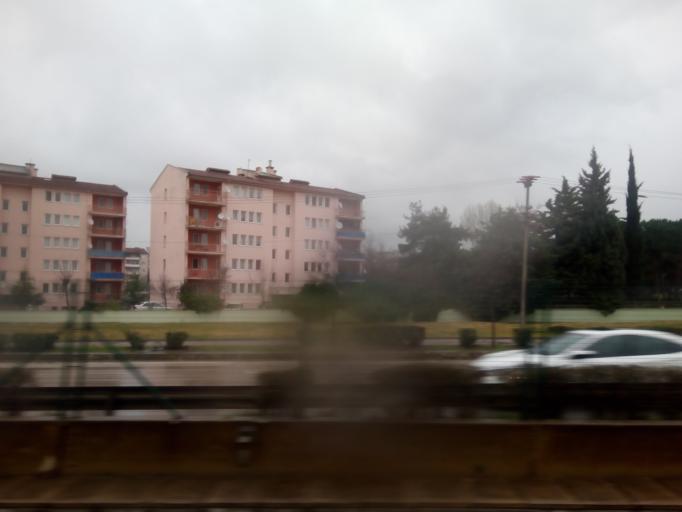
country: TR
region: Bursa
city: Niluefer
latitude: 40.2447
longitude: 28.9654
